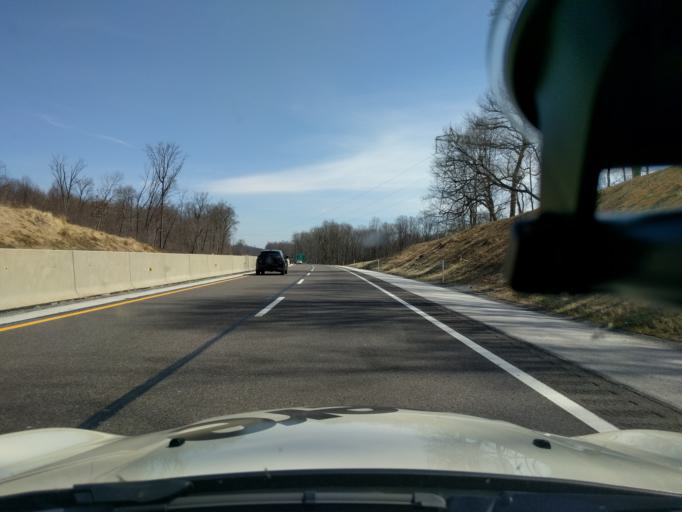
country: US
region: Pennsylvania
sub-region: Lebanon County
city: Cornwall
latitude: 40.2264
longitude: -76.4787
